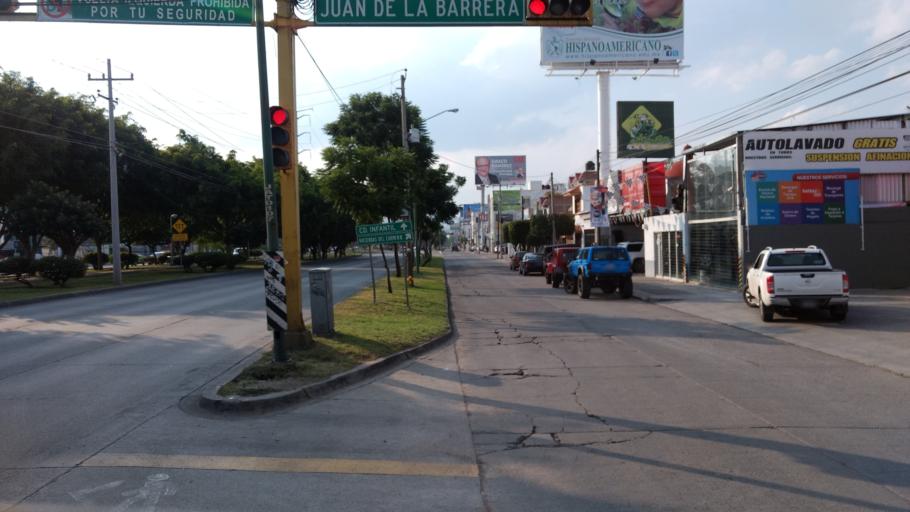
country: MX
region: Guanajuato
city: Leon
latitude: 21.1521
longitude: -101.6728
